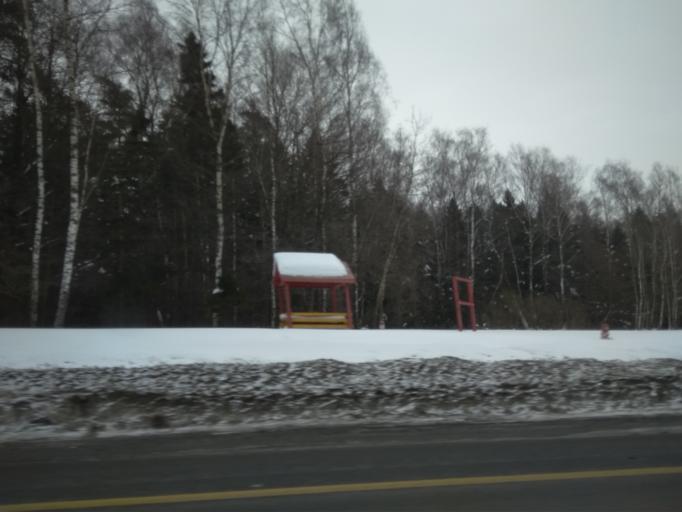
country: RU
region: Moskovskaya
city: Vostryakovo
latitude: 55.4563
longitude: 37.8557
